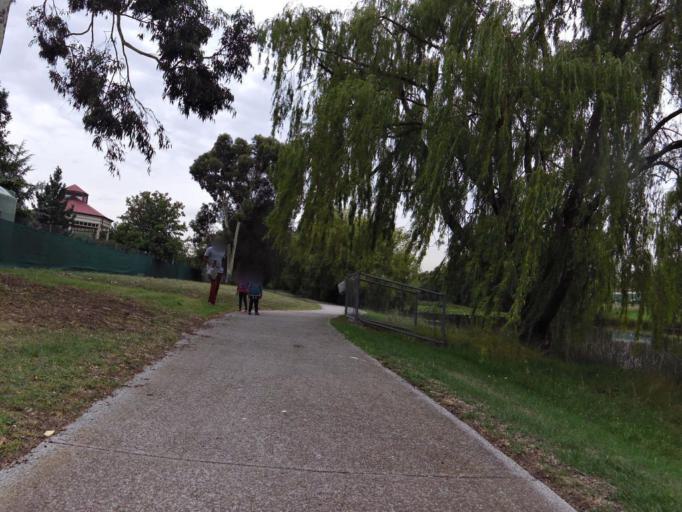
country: AU
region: Victoria
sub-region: Brimbank
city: Keilor Lodge
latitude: -37.7040
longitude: 144.8027
